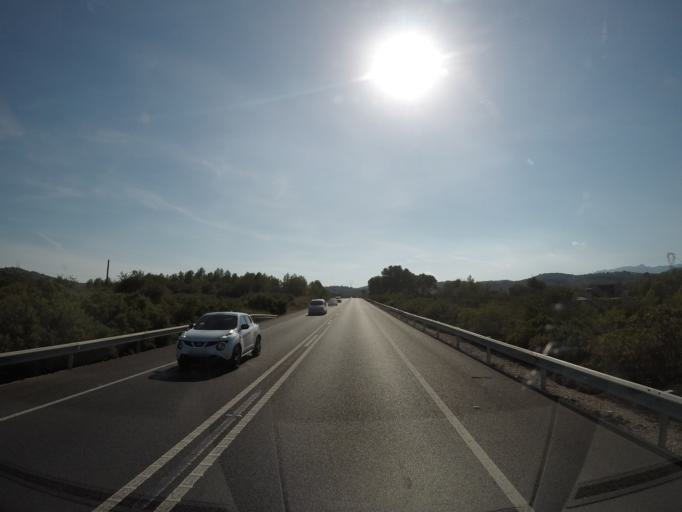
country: ES
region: Catalonia
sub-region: Provincia de Tarragona
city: El Perello
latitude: 40.8919
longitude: 0.7254
